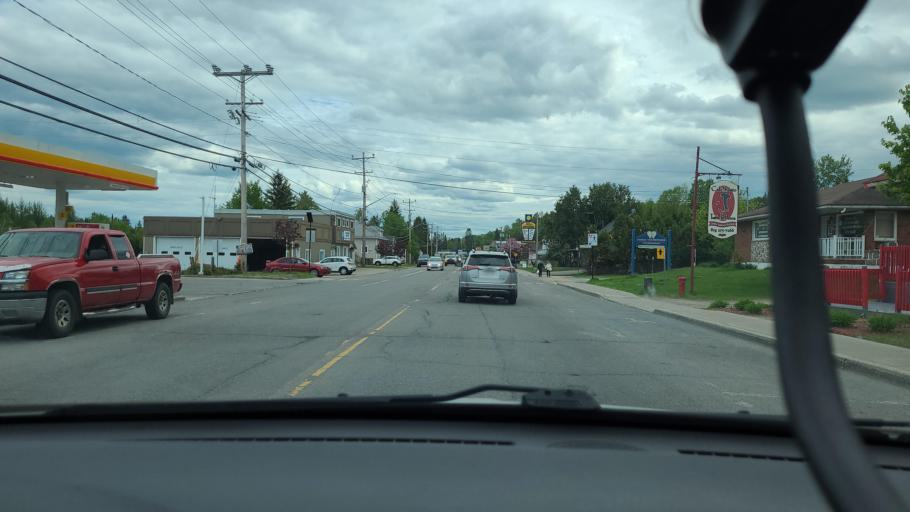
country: CA
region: Quebec
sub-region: Laurentides
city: Riviere-Rouge
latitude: 46.4046
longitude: -74.8668
